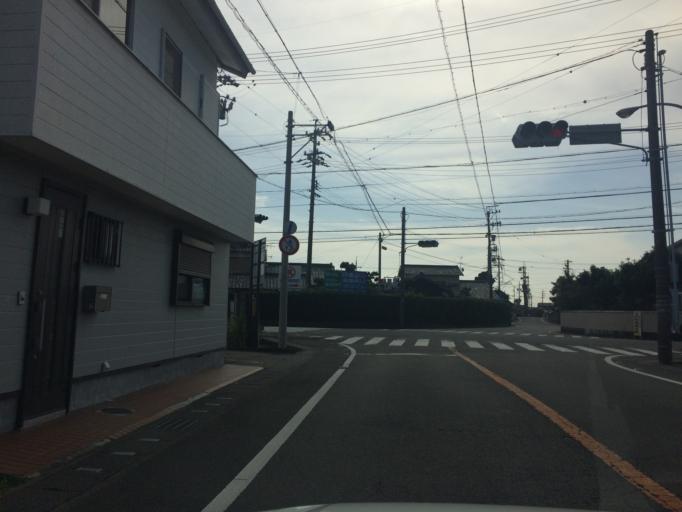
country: JP
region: Shizuoka
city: Yaizu
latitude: 34.8181
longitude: 138.3161
